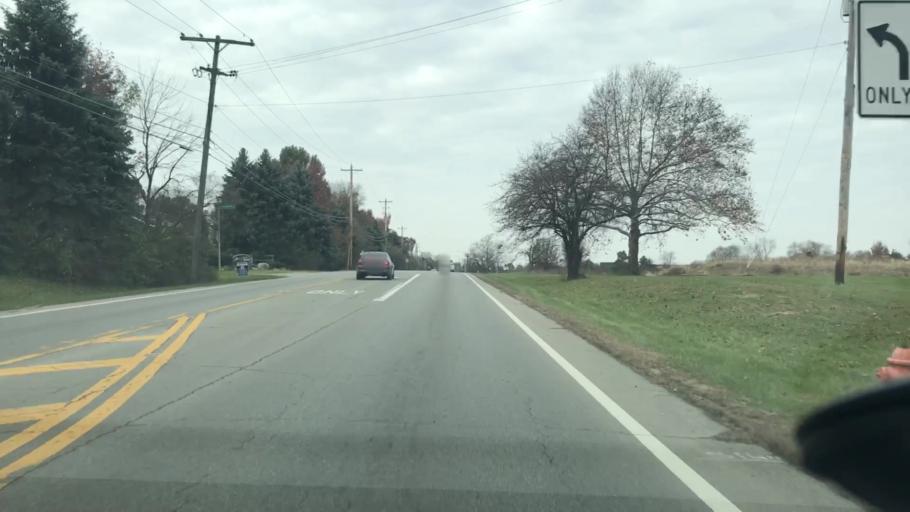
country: US
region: Ohio
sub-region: Franklin County
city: Upper Arlington
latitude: 39.9897
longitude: -83.1011
